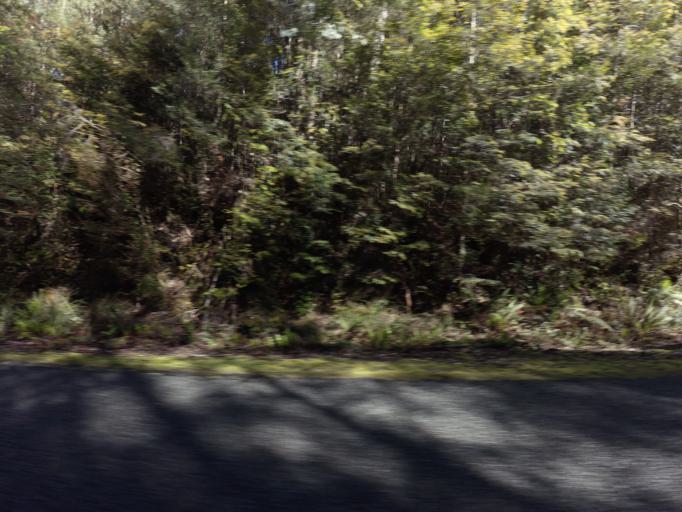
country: AU
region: Tasmania
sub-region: Derwent Valley
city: New Norfolk
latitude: -42.7466
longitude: 146.4140
